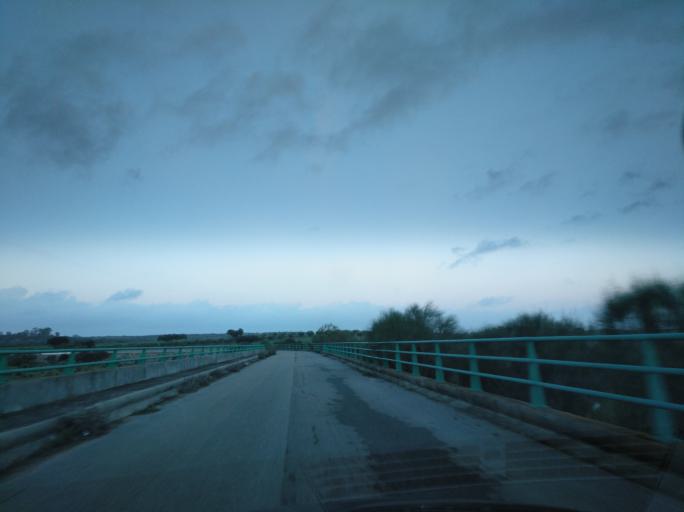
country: PT
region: Portalegre
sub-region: Campo Maior
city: Campo Maior
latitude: 39.0996
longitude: -7.1199
